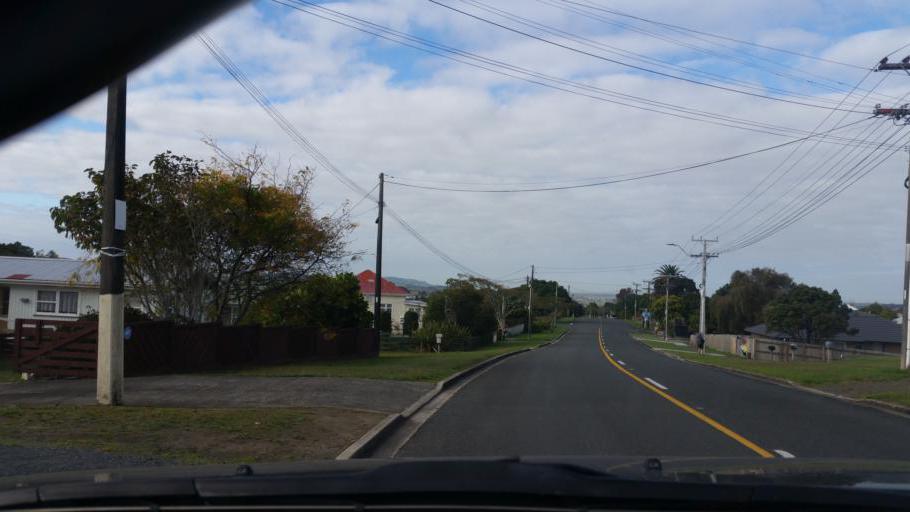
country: NZ
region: Northland
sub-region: Kaipara District
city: Dargaville
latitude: -35.9297
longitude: 173.8706
